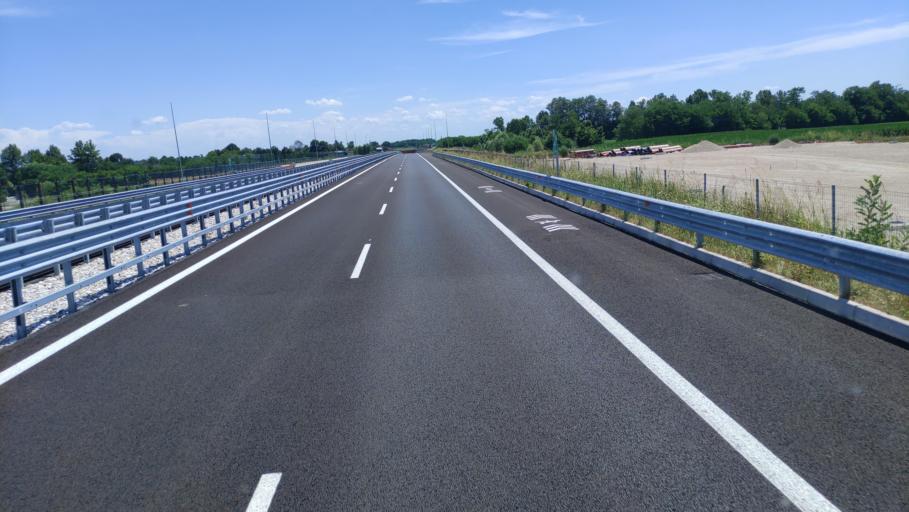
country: IT
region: Veneto
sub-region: Provincia di Treviso
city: San Vito
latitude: 45.7524
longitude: 11.8966
